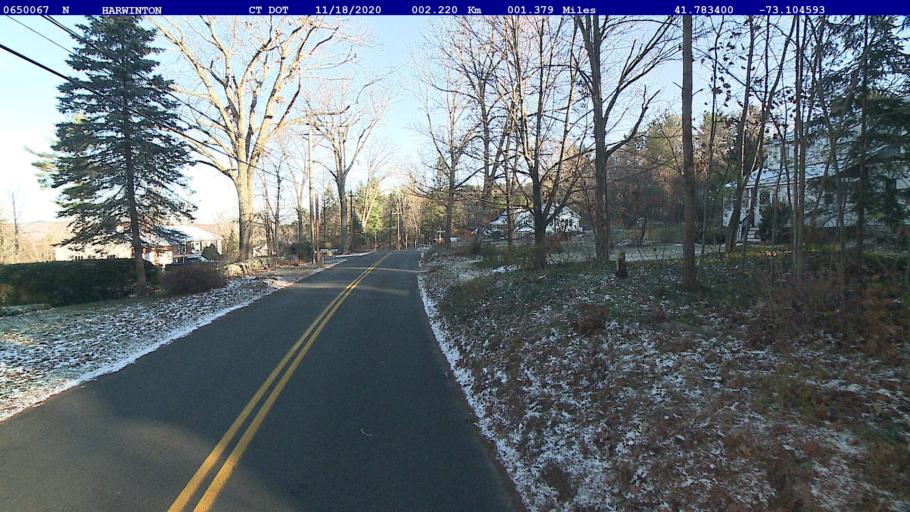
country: US
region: Connecticut
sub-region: Litchfield County
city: Torrington
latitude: 41.7834
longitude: -73.1046
